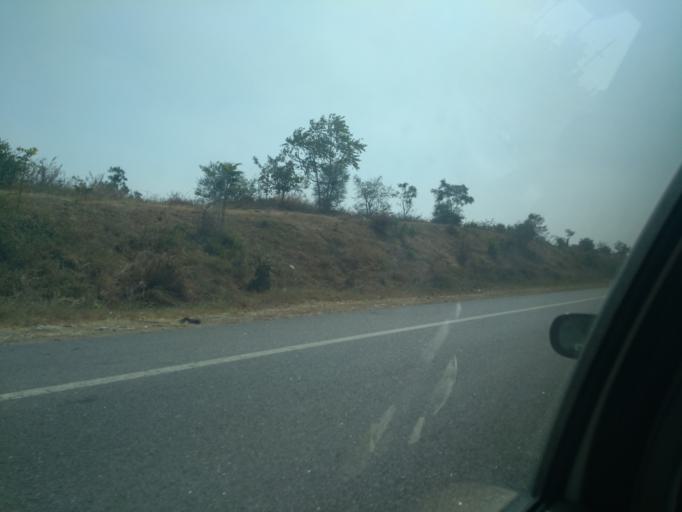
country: IN
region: Telangana
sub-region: Mahbubnagar
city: Mahbubnagar
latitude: 16.7442
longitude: 78.1018
